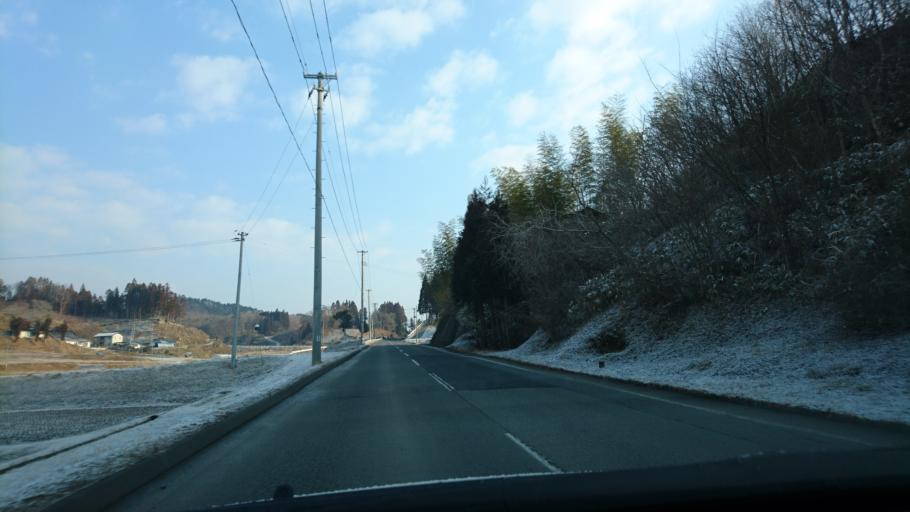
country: JP
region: Iwate
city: Ichinoseki
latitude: 38.9090
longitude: 141.3773
